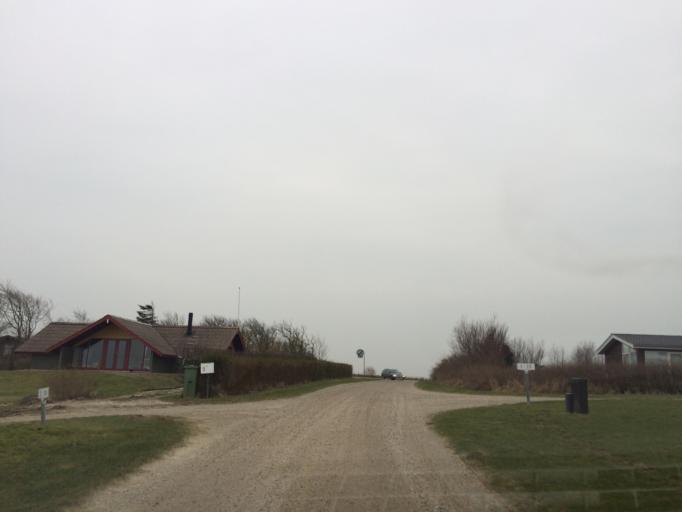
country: DK
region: Central Jutland
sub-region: Lemvig Kommune
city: Lemvig
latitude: 56.5756
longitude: 8.2777
